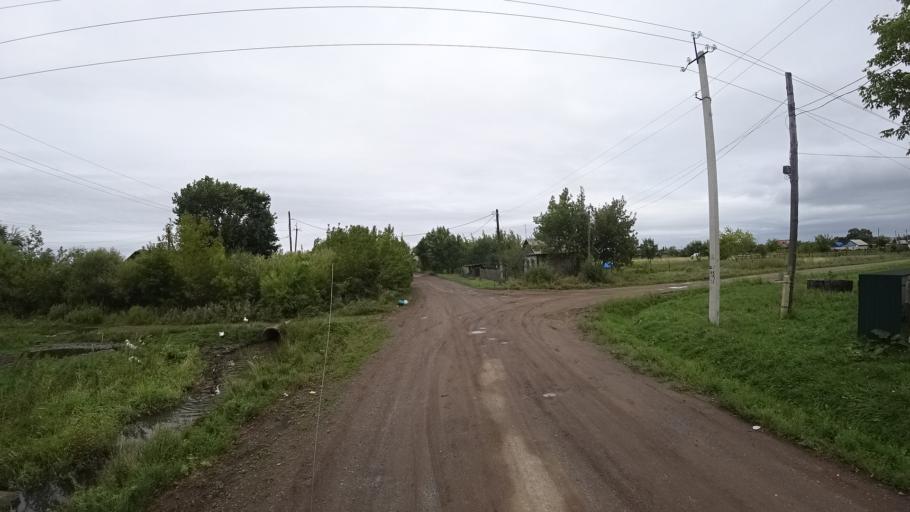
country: RU
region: Primorskiy
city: Chernigovka
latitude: 44.3371
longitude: 132.5597
